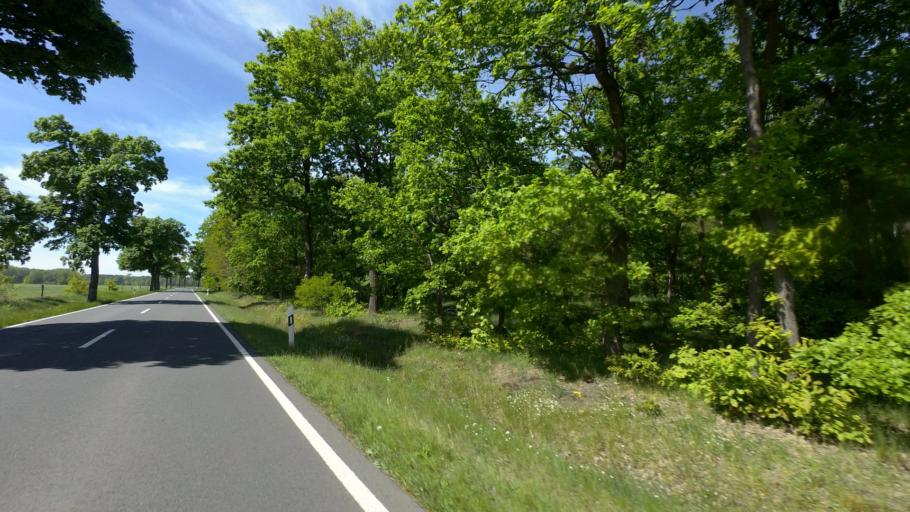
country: DE
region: Brandenburg
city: Baruth
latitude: 52.0626
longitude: 13.4950
